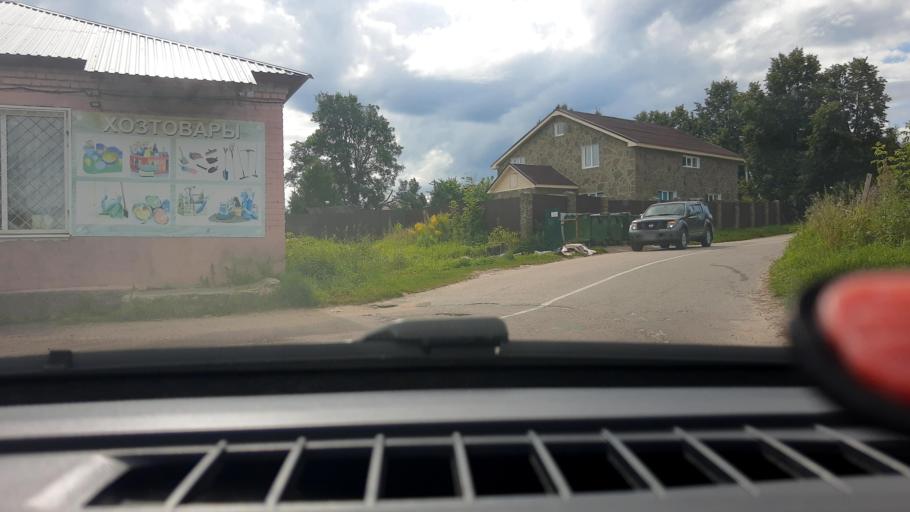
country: RU
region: Nizjnij Novgorod
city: Burevestnik
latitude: 56.0332
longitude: 43.7193
